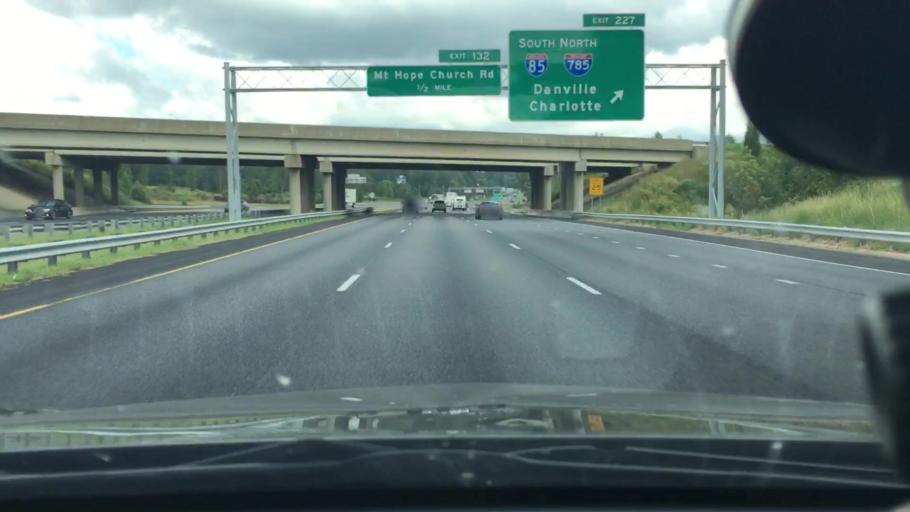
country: US
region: North Carolina
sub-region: Guilford County
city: McLeansville
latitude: 36.0594
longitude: -79.6872
